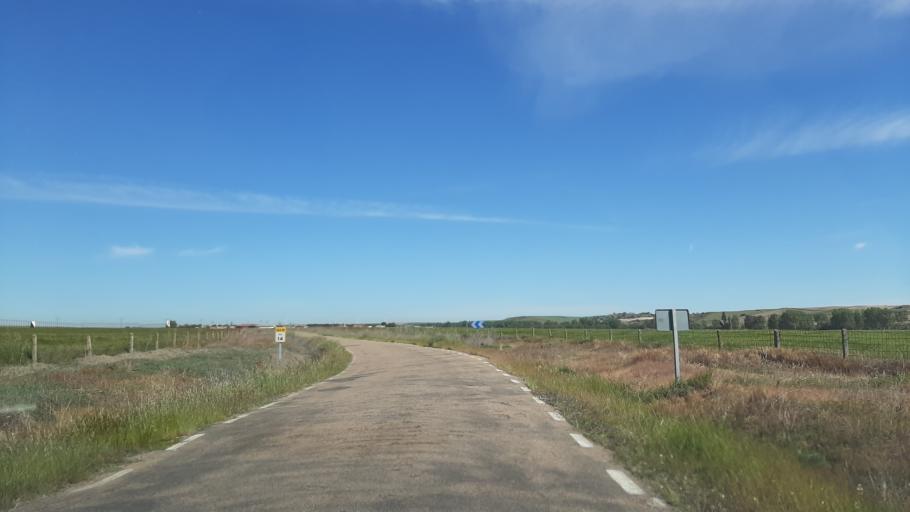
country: ES
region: Castille and Leon
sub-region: Provincia de Salamanca
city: Gajates
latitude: 40.7988
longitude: -5.3740
